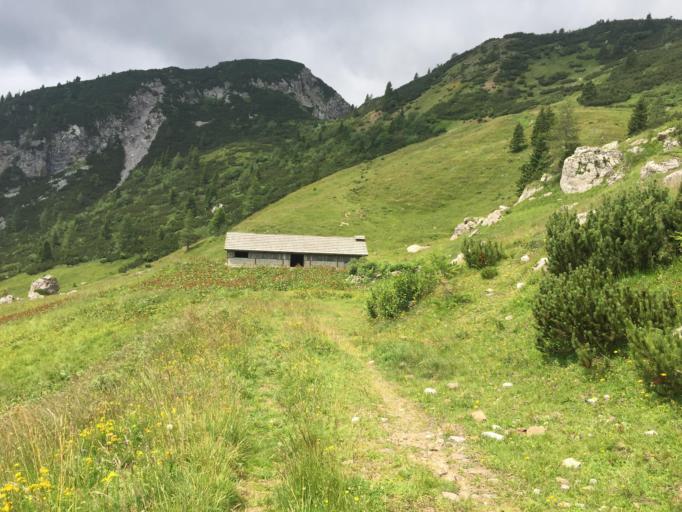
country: AT
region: Carinthia
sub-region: Politischer Bezirk Hermagor
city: Kirchbach
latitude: 46.5619
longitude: 13.2035
